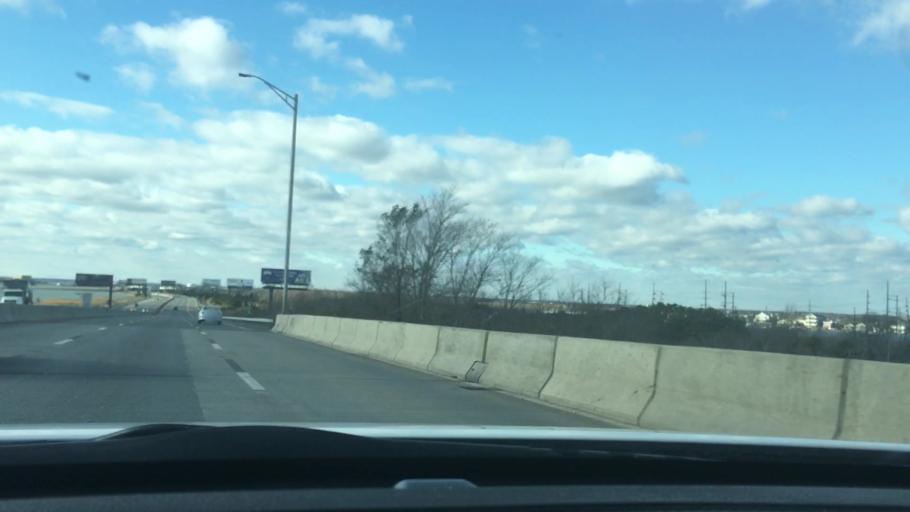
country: US
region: New Jersey
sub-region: Atlantic County
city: Atlantic City
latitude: 39.3642
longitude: -74.4468
